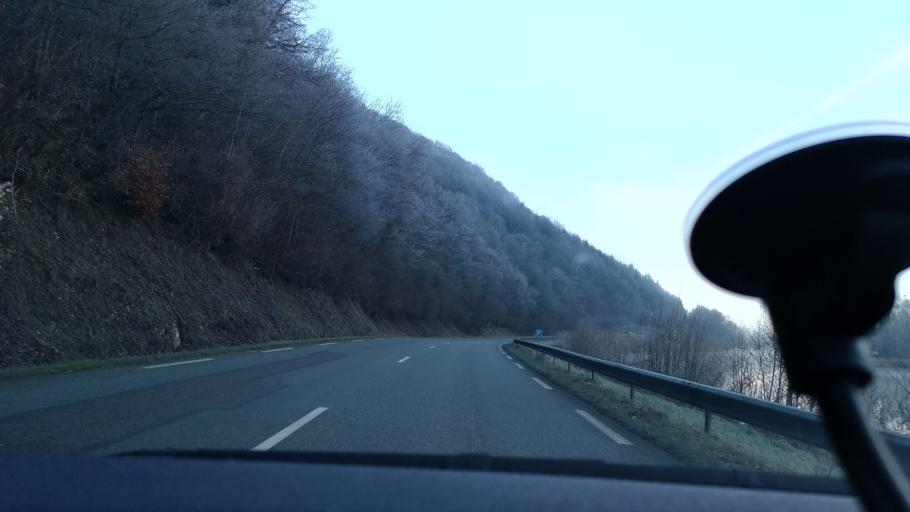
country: FR
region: Franche-Comte
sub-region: Departement du Doubs
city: Clerval
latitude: 47.3979
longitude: 6.5079
